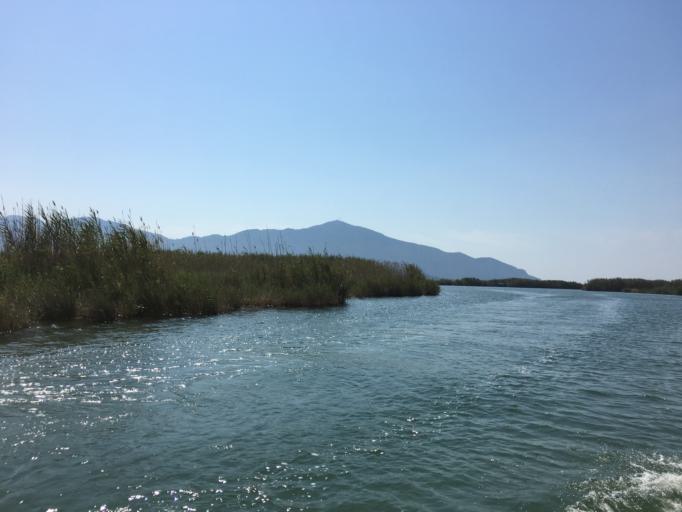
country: TR
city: Dalyan
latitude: 36.8172
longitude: 28.6343
